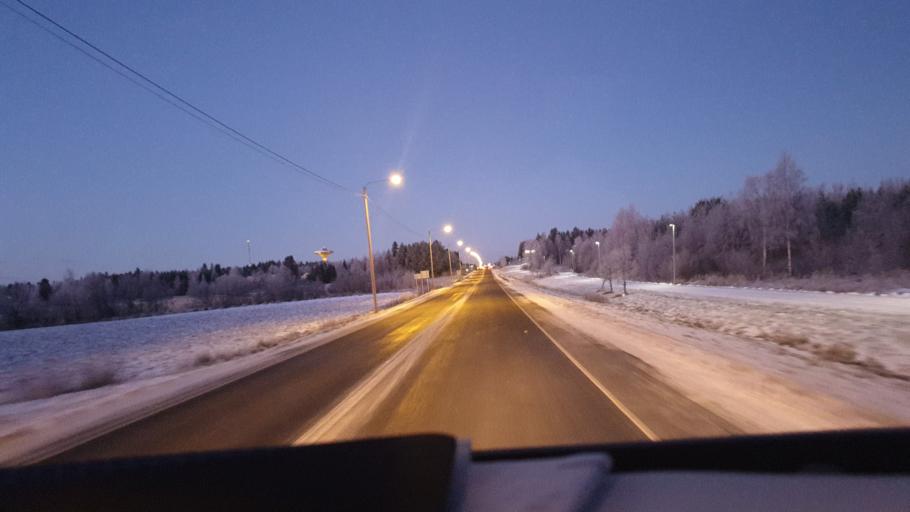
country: FI
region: Northern Ostrobothnia
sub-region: Raahe
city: Raahe
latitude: 64.6874
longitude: 24.5872
